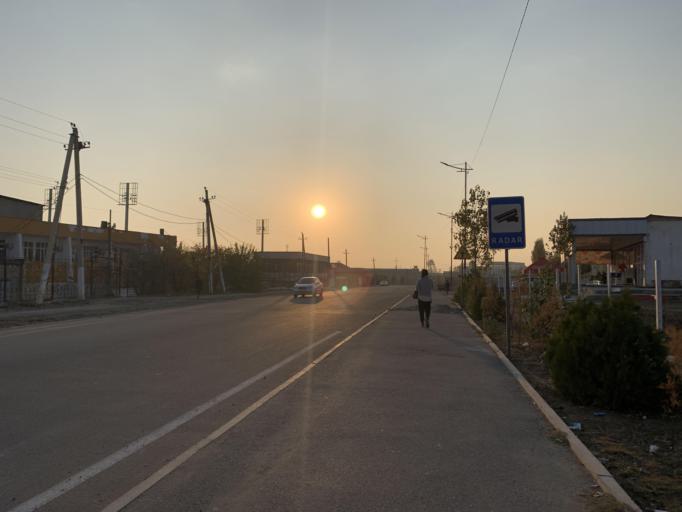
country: UZ
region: Namangan
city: Namangan Shahri
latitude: 41.0023
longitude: 71.6020
